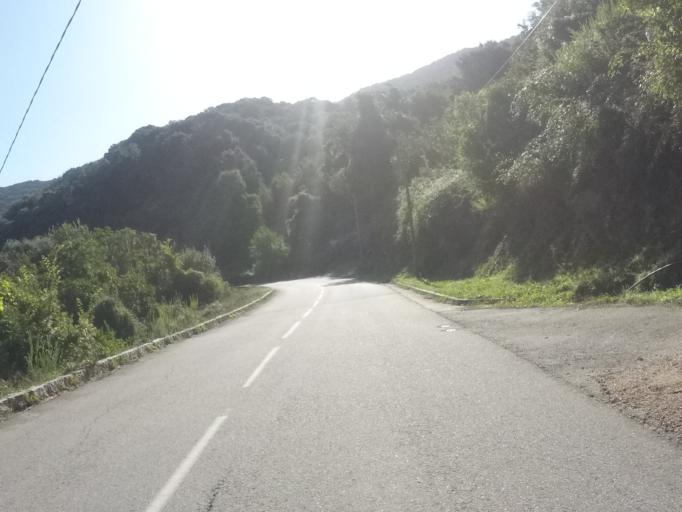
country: FR
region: Corsica
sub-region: Departement de la Corse-du-Sud
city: Olmeto
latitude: 41.7454
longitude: 8.9046
